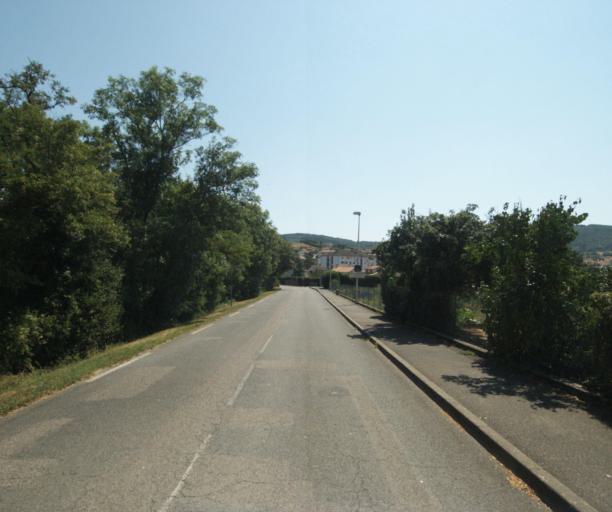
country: FR
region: Rhone-Alpes
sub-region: Departement du Rhone
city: Saint-Pierre-la-Palud
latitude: 45.7922
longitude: 4.6082
